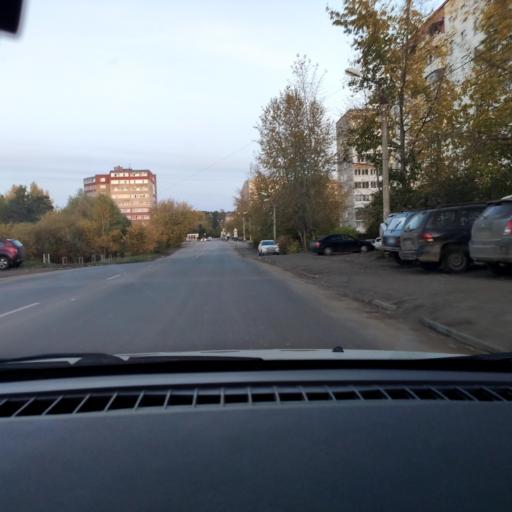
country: RU
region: Perm
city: Overyata
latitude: 58.0274
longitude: 55.8365
